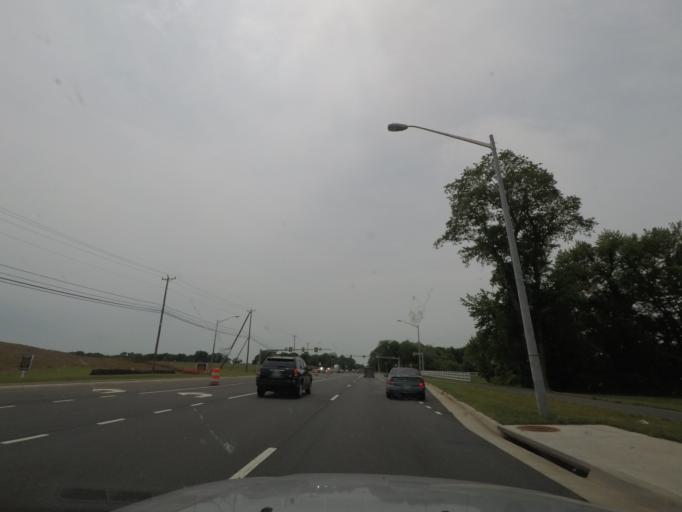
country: US
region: Virginia
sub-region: Loudoun County
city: Leesburg
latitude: 39.0922
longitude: -77.5836
